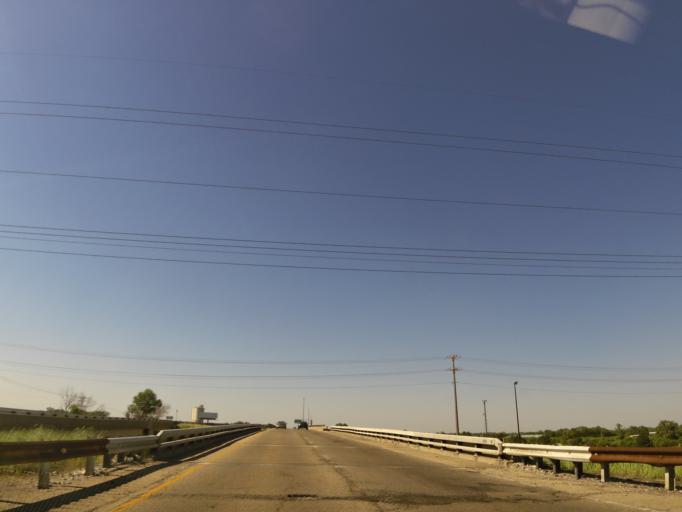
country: US
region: Illinois
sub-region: Winnebago County
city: South Beloit
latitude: 42.4560
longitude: -89.0194
